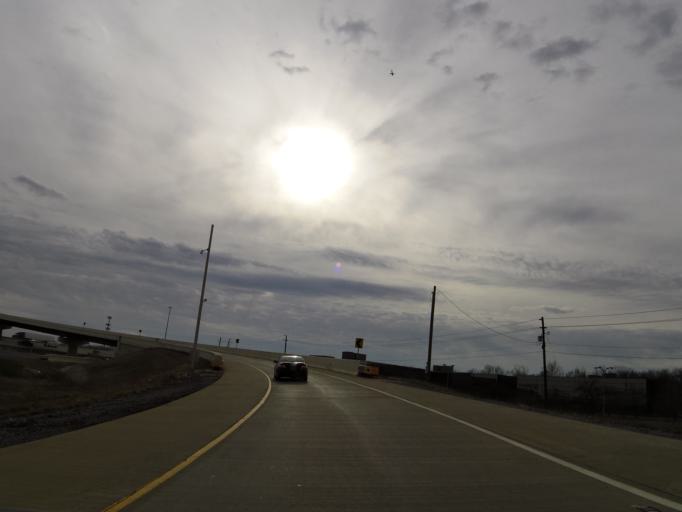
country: US
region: Indiana
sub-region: Marion County
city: Speedway
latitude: 39.8049
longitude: -86.2773
